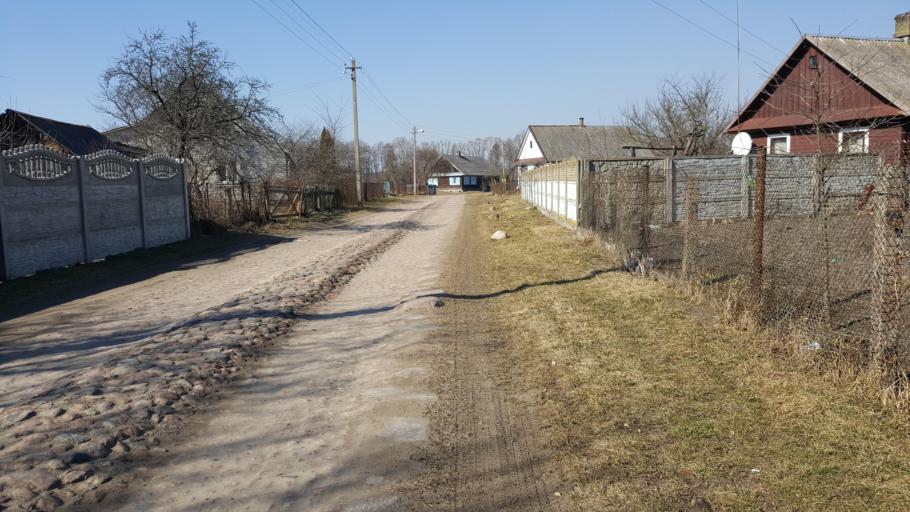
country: BY
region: Brest
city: Kamyanyets
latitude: 52.3565
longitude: 23.7502
